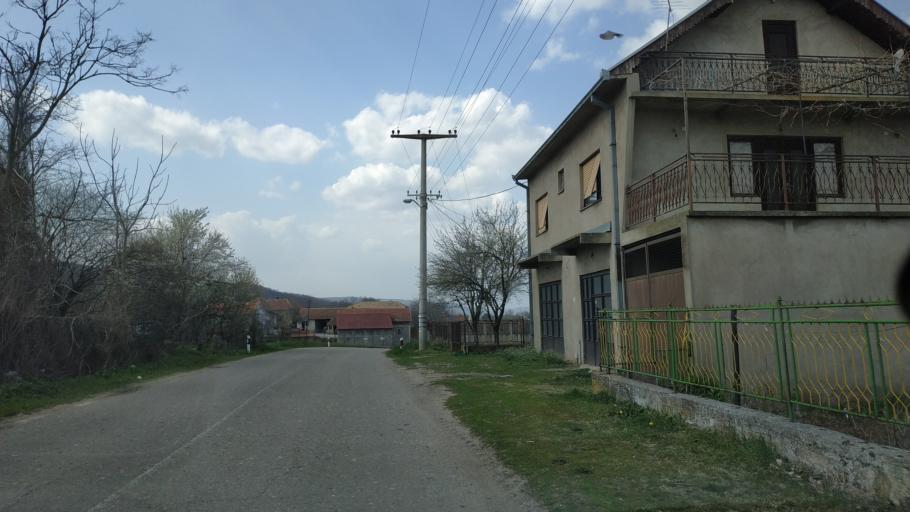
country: RS
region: Central Serbia
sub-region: Nisavski Okrug
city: Aleksinac
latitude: 43.5550
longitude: 21.6114
